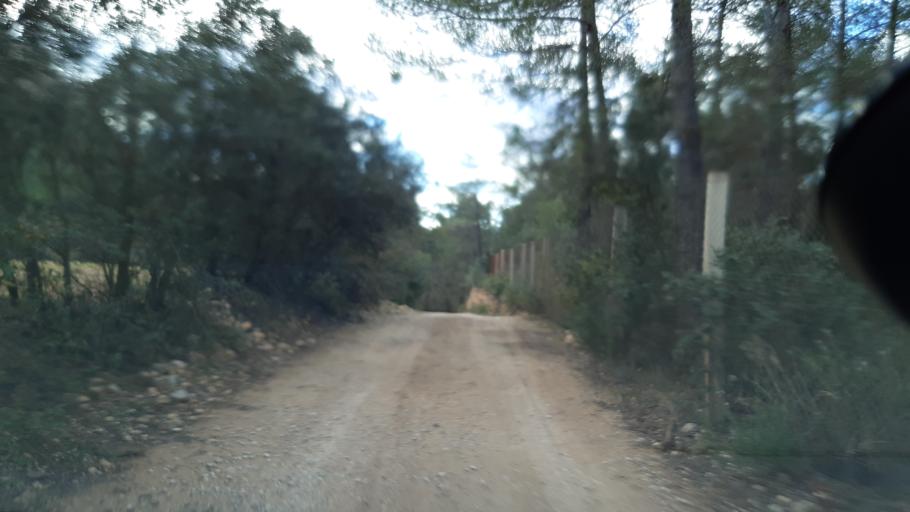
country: ES
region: Aragon
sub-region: Provincia de Teruel
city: Valderrobres
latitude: 40.8528
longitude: 0.2254
